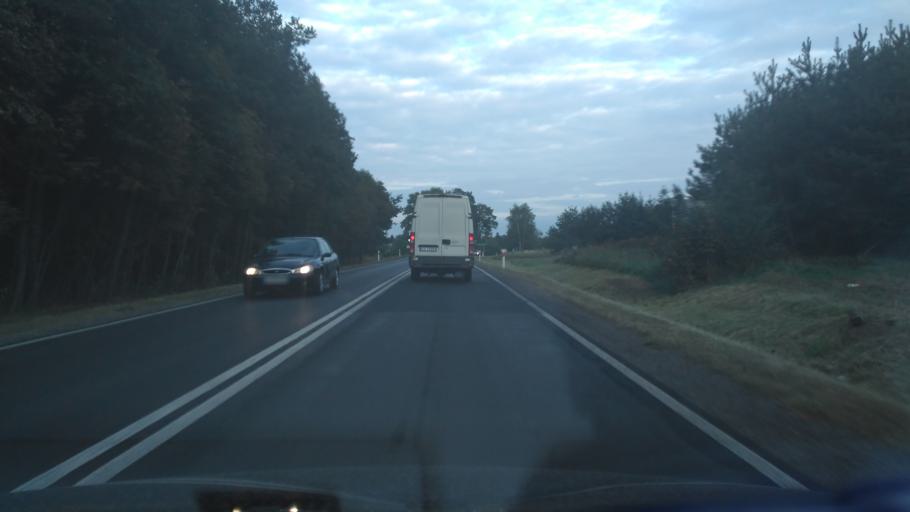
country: PL
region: Lublin Voivodeship
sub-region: Powiat leczynski
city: Spiczyn
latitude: 51.3010
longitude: 22.7527
